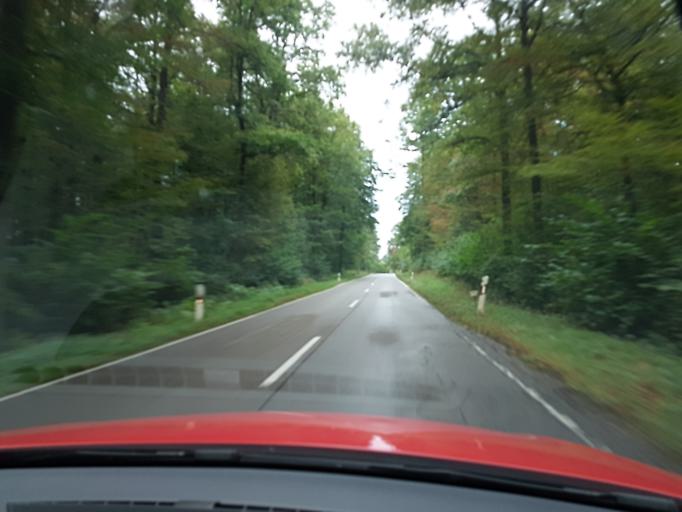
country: DE
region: Baden-Wuerttemberg
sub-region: Regierungsbezirk Stuttgart
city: Pfaffenhofen
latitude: 49.0384
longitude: 8.9753
